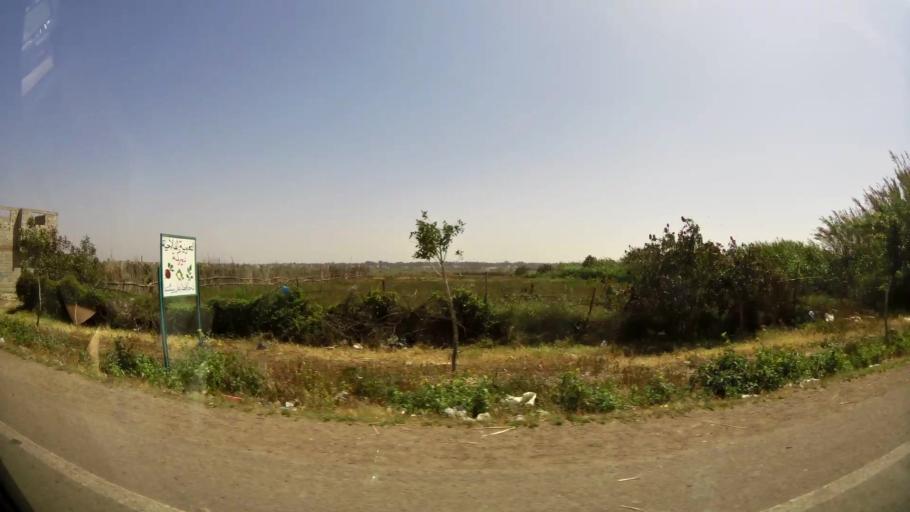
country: MA
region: Souss-Massa-Draa
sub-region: Inezgane-Ait Mellou
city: Inezgane
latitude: 30.3429
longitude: -9.5399
